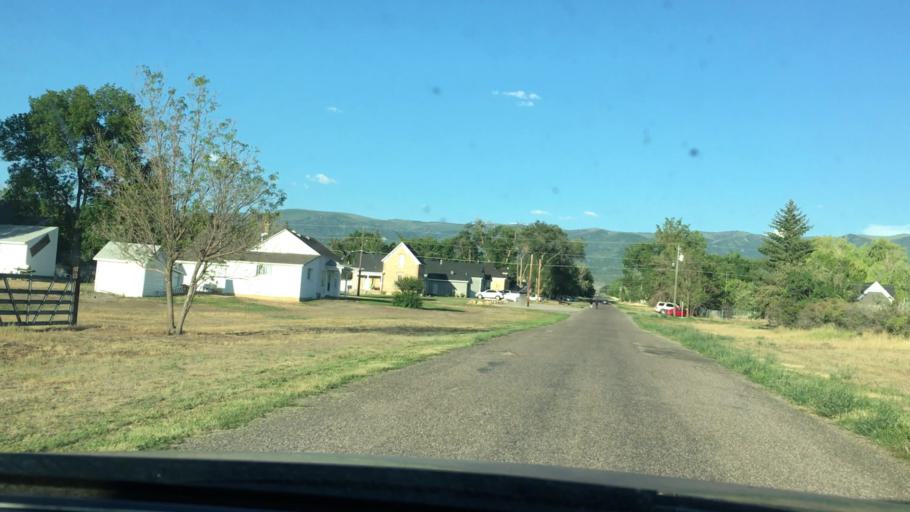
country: US
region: Utah
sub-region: Sanpete County
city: Mount Pleasant
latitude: 39.5409
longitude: -111.4622
